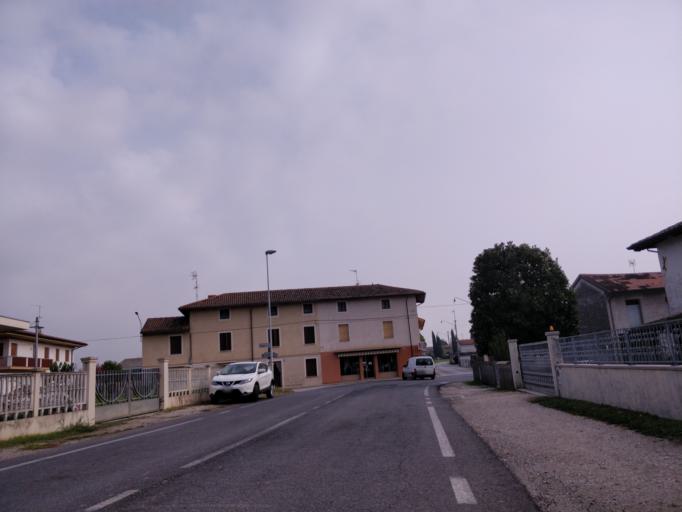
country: IT
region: Friuli Venezia Giulia
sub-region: Provincia di Udine
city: Bertiolo
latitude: 45.9438
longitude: 13.0471
